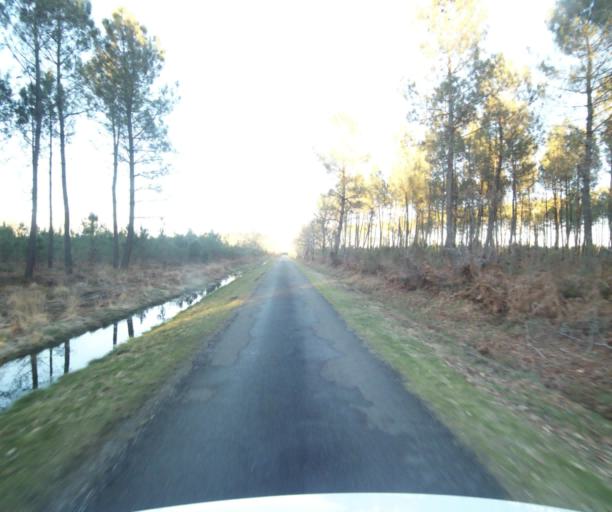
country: FR
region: Aquitaine
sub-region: Departement des Landes
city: Gabarret
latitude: 44.1169
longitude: -0.0254
